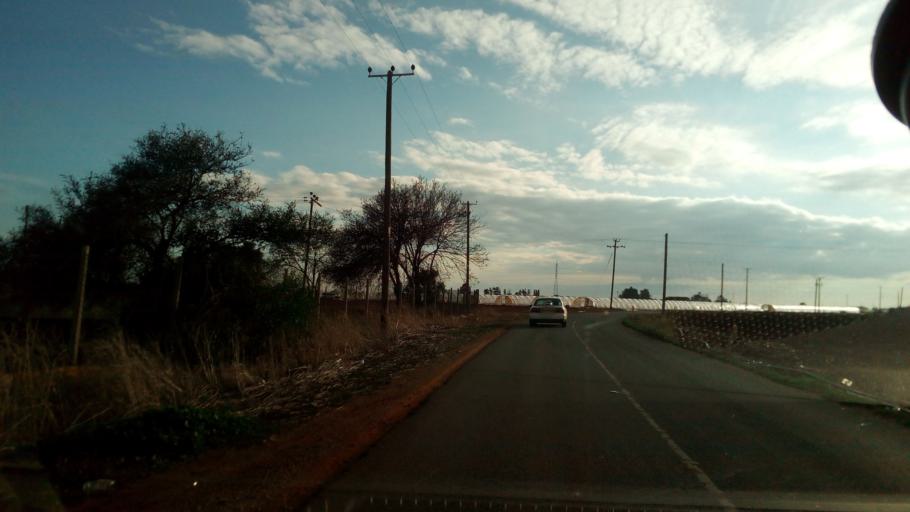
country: CY
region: Ammochostos
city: Avgorou
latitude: 35.0062
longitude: 33.8030
